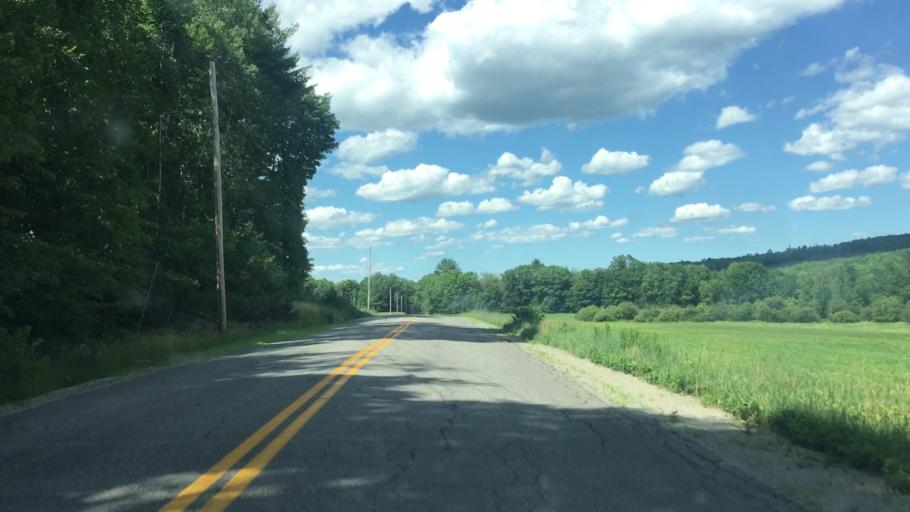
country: US
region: Maine
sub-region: Franklin County
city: Chesterville
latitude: 44.5820
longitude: -70.0899
